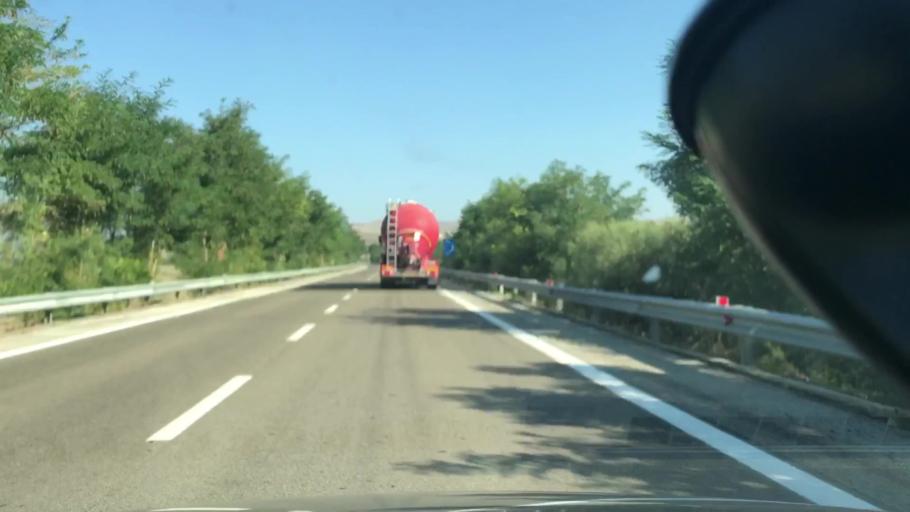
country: IT
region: Basilicate
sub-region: Provincia di Matera
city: Irsina
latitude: 40.8015
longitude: 16.2743
